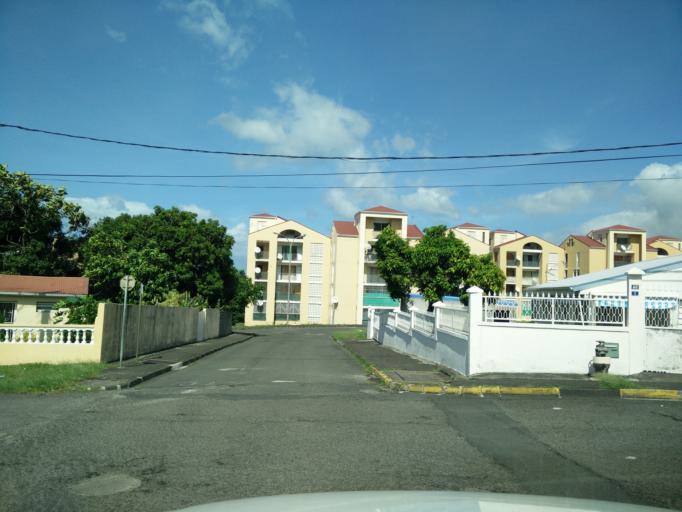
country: GP
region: Guadeloupe
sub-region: Guadeloupe
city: Basse-Terre
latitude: 15.9980
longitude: -61.7175
